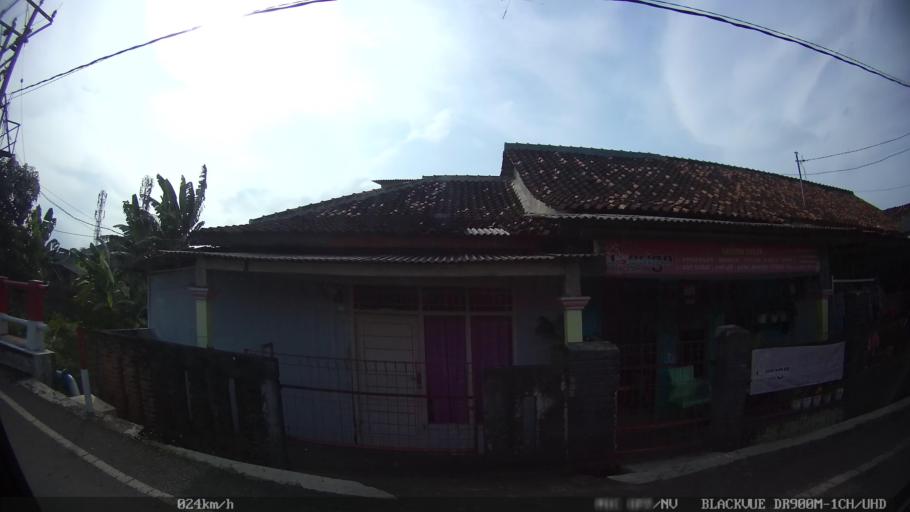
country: ID
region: Lampung
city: Kedaton
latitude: -5.4011
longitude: 105.2635
